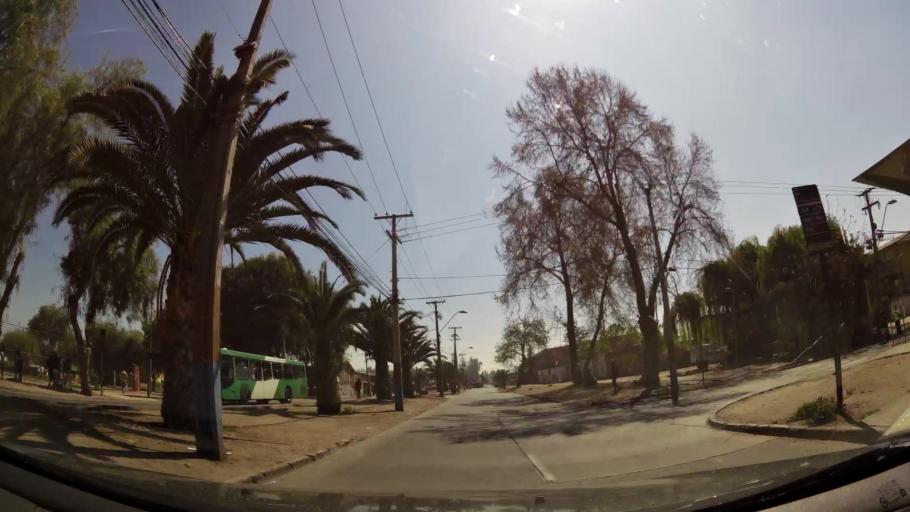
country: CL
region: Santiago Metropolitan
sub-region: Provincia de Santiago
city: Lo Prado
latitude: -33.3637
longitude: -70.7532
